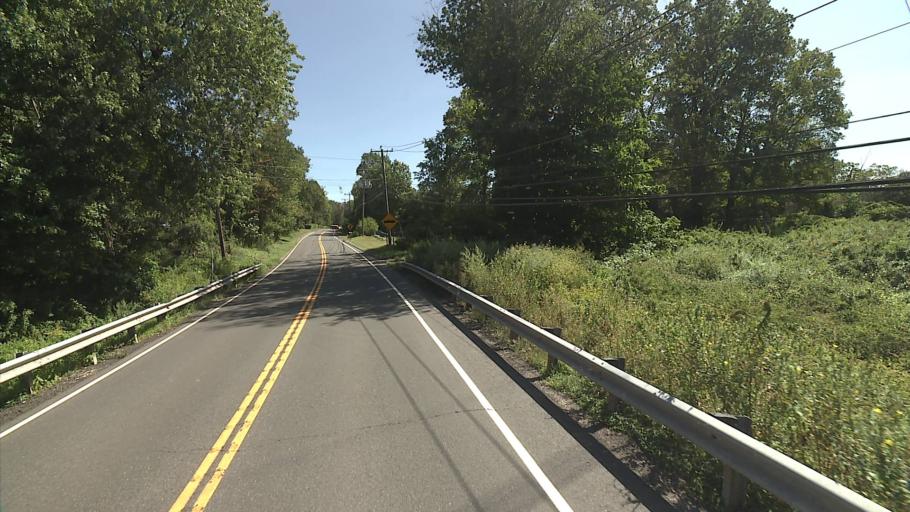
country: US
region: Connecticut
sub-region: New Haven County
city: Oxford
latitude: 41.4215
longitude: -73.1530
